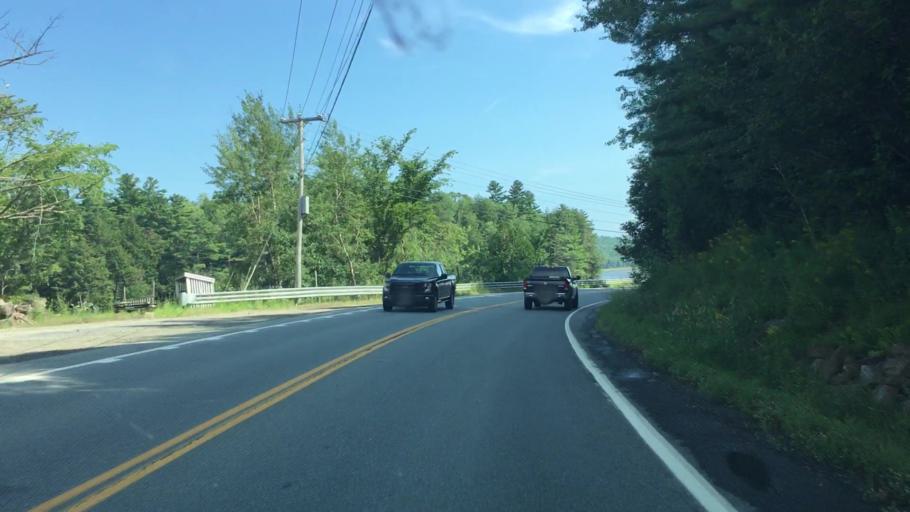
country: US
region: Maine
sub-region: Waldo County
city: Frankfort
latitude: 44.6024
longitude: -68.8684
